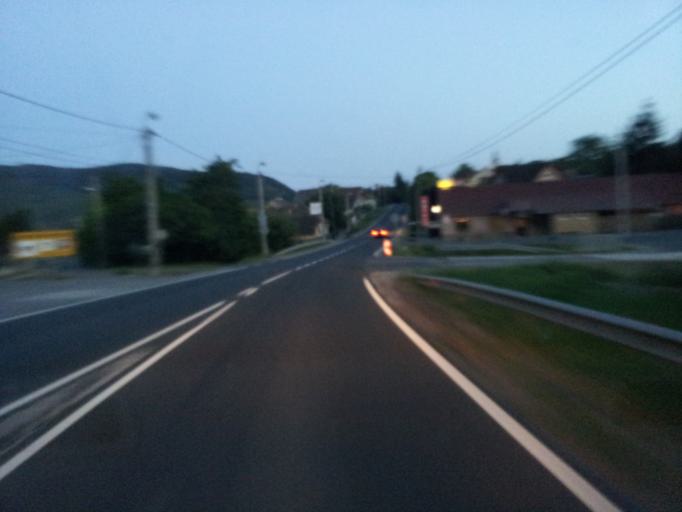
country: HU
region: Nograd
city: Retsag
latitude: 47.8592
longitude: 19.1062
